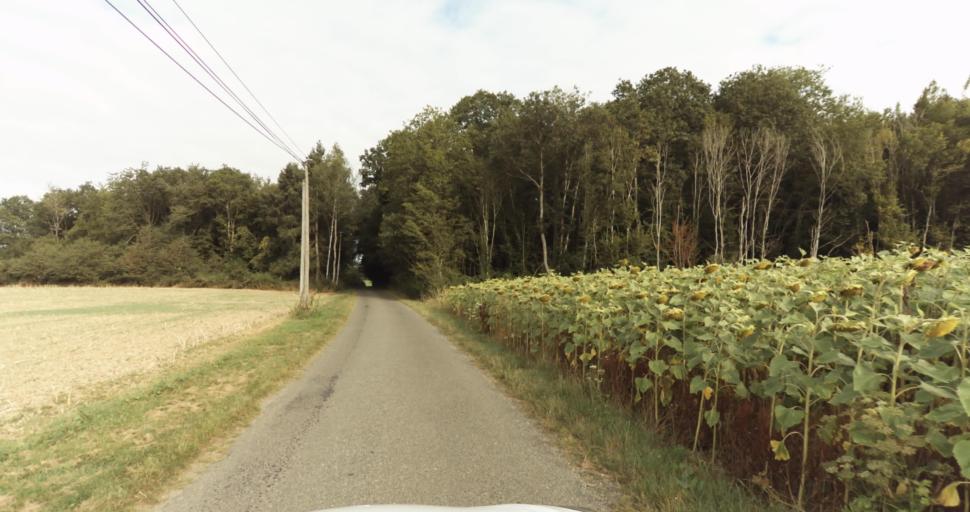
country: FR
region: Haute-Normandie
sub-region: Departement de l'Eure
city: Saint-Germain-sur-Avre
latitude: 48.8295
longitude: 1.2529
